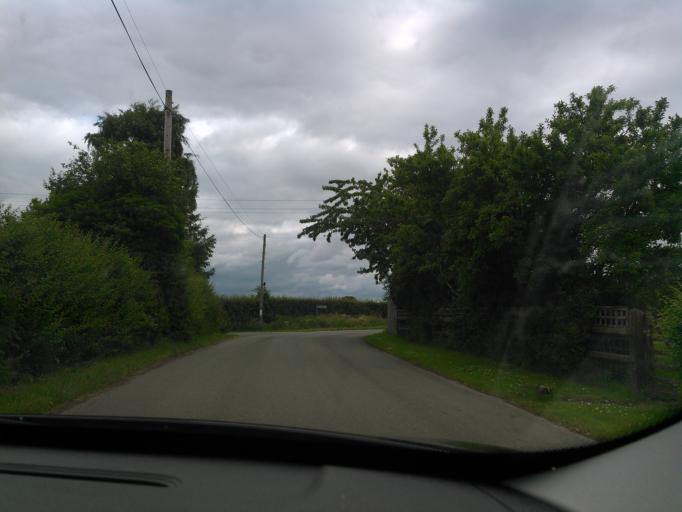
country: GB
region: England
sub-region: Shropshire
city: Wem
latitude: 52.9036
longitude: -2.7629
